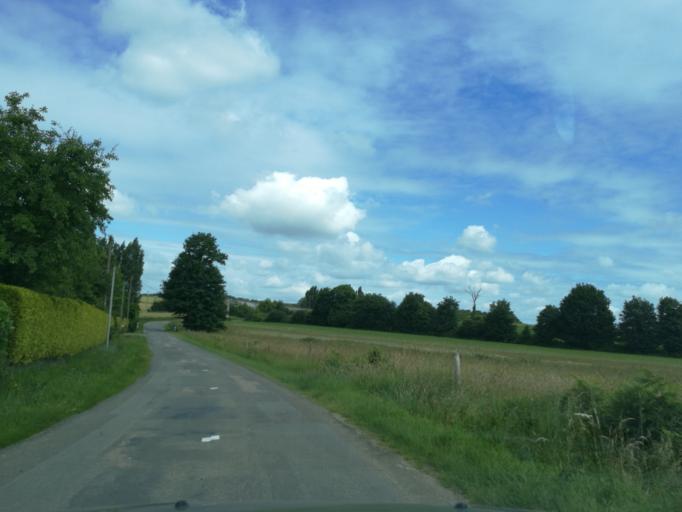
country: FR
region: Brittany
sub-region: Departement d'Ille-et-Vilaine
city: Bedee
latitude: 48.1804
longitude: -1.9841
